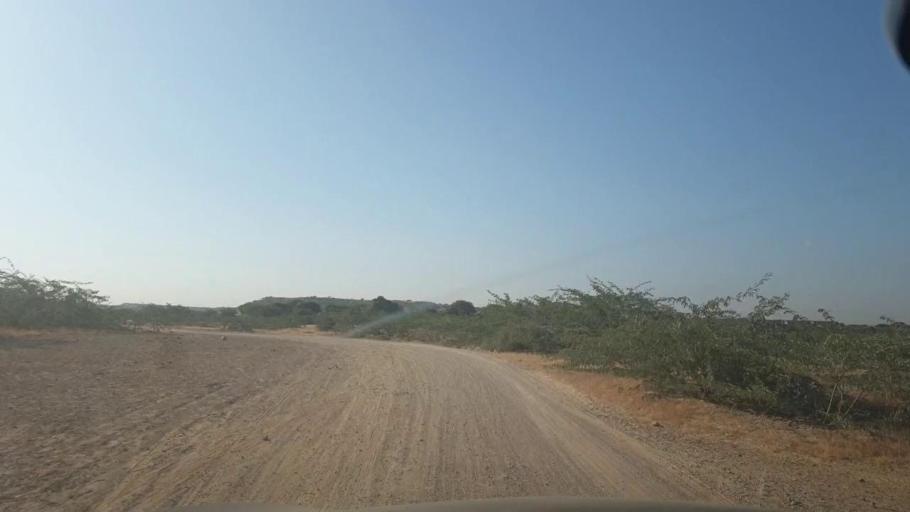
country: PK
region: Sindh
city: Malir Cantonment
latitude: 25.0370
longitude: 67.2607
